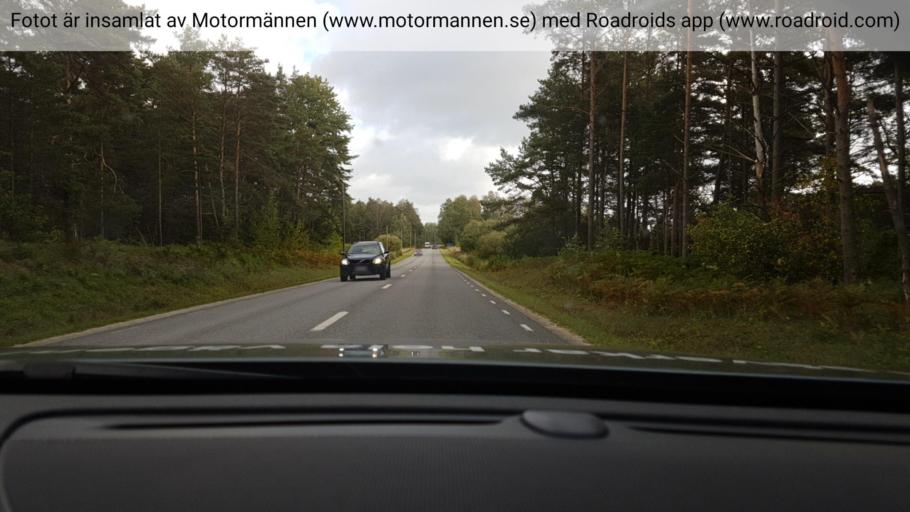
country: SE
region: Gotland
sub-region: Gotland
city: Visby
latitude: 57.6585
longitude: 18.4103
